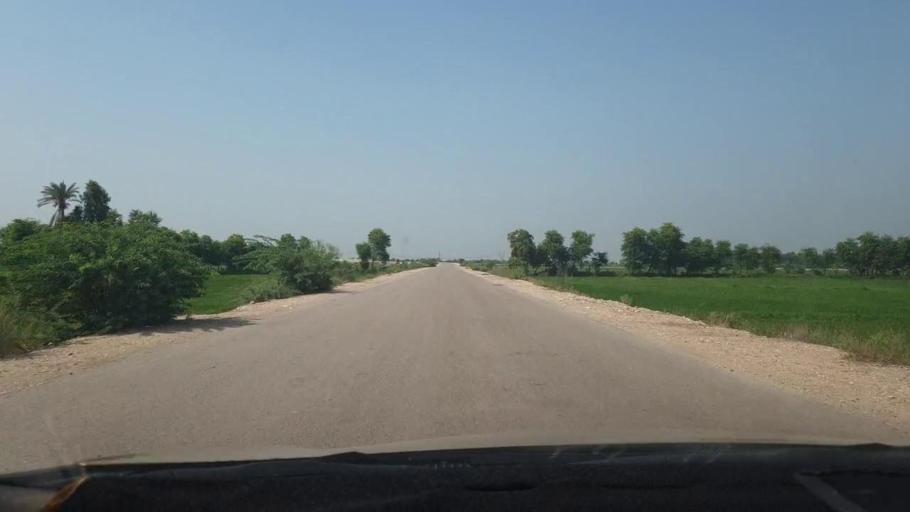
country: PK
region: Sindh
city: Larkana
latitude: 27.5999
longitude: 68.2431
